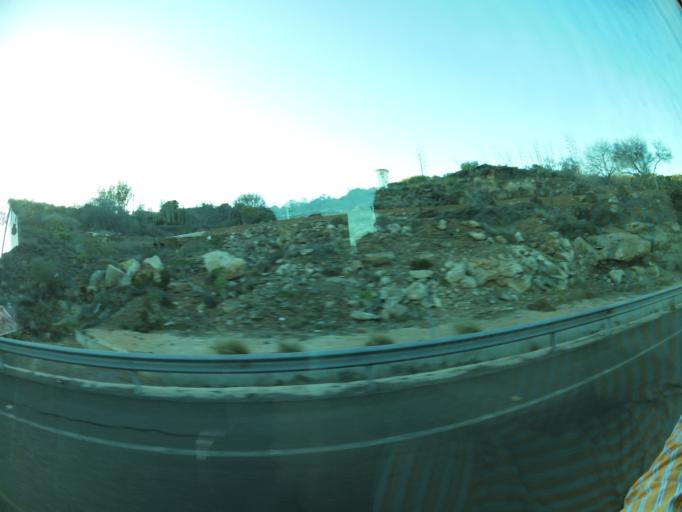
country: ES
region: Canary Islands
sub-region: Provincia de Las Palmas
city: Playa del Ingles
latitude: 27.7750
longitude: -15.5332
